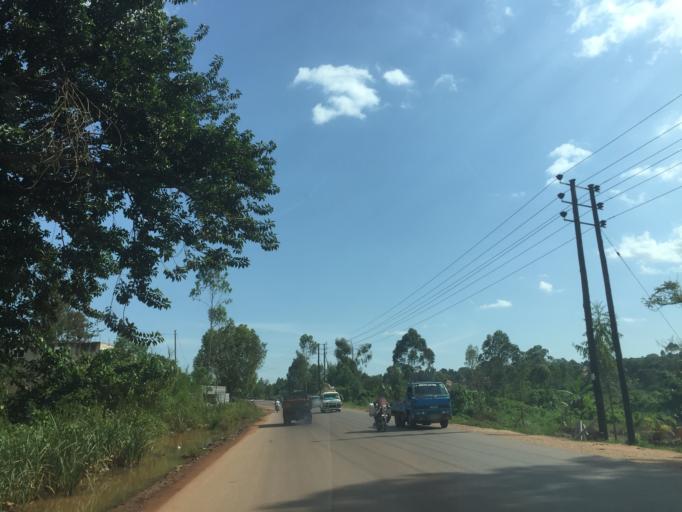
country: UG
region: Central Region
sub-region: Wakiso District
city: Wakiso
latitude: 0.4280
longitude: 32.5346
